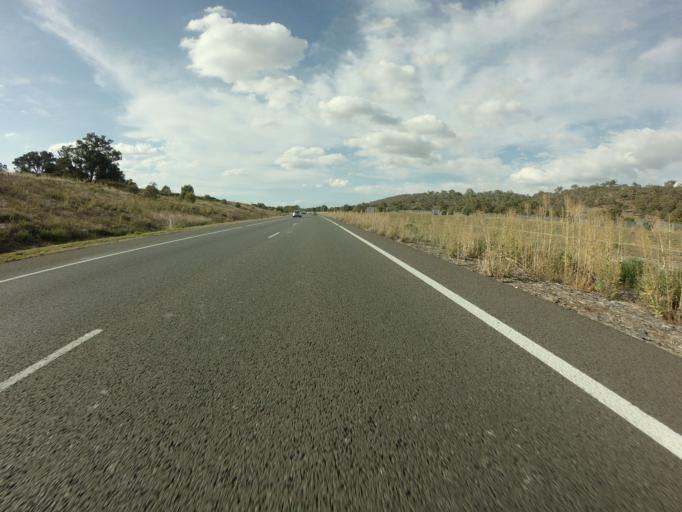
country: AU
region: Australian Capital Territory
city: Canberra
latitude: -35.2328
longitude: 149.1955
